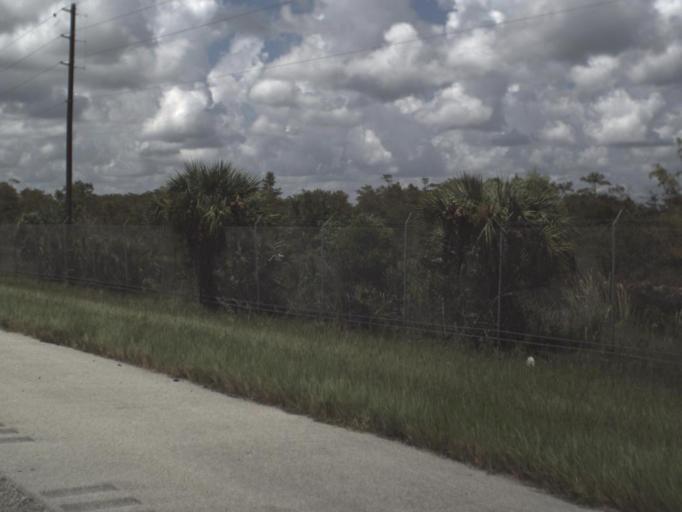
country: US
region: Florida
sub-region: Broward County
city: Weston
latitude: 26.1727
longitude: -80.8886
